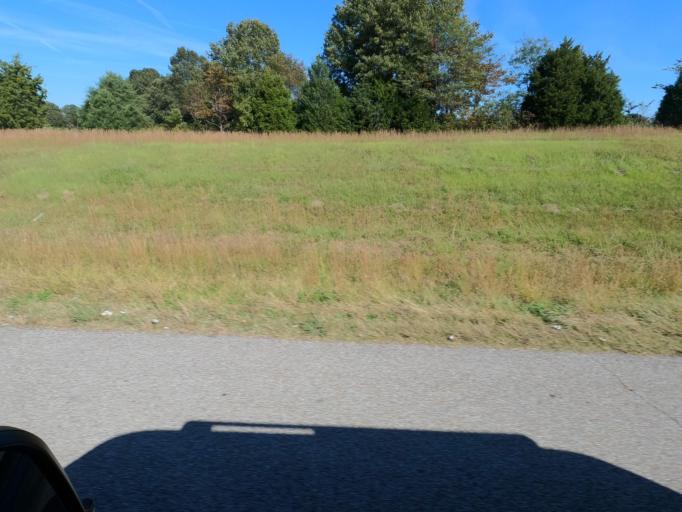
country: US
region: Tennessee
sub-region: Crockett County
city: Alamo
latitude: 35.7886
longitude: -89.1522
